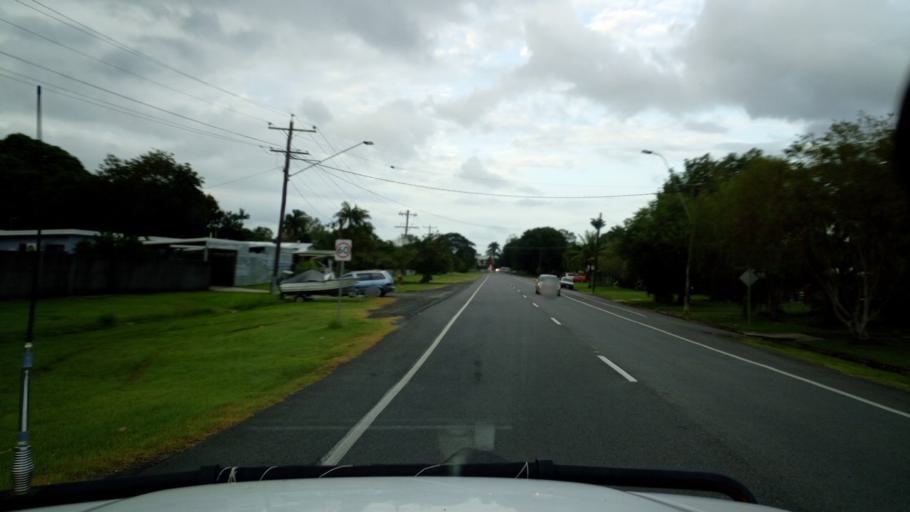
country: AU
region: Queensland
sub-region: Cairns
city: Woree
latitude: -16.9310
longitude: 145.7383
